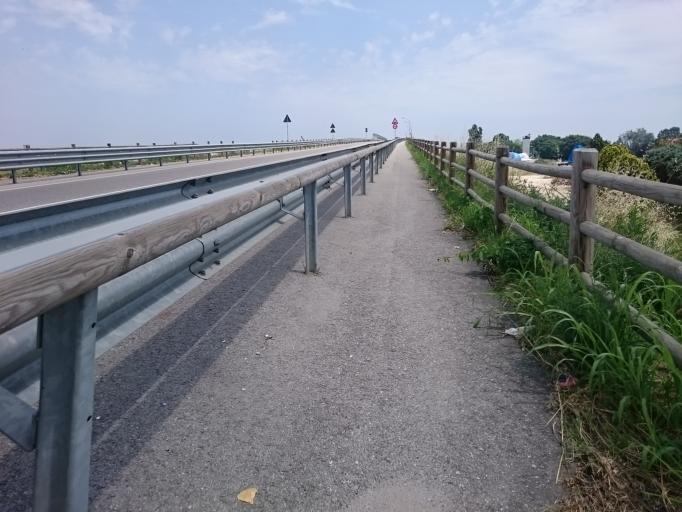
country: IT
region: Veneto
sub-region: Provincia di Venezia
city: Sant'Anna
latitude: 45.1836
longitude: 12.2679
